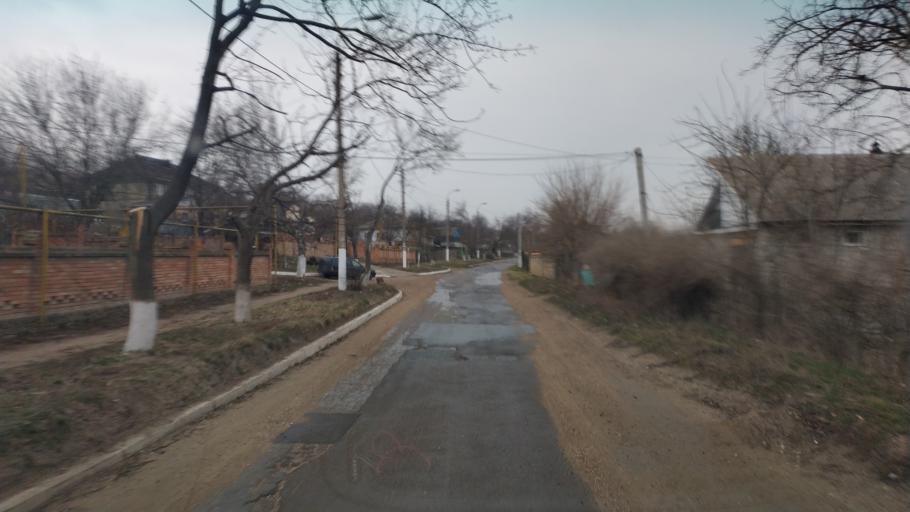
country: MD
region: Chisinau
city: Singera
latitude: 46.8313
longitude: 28.9776
